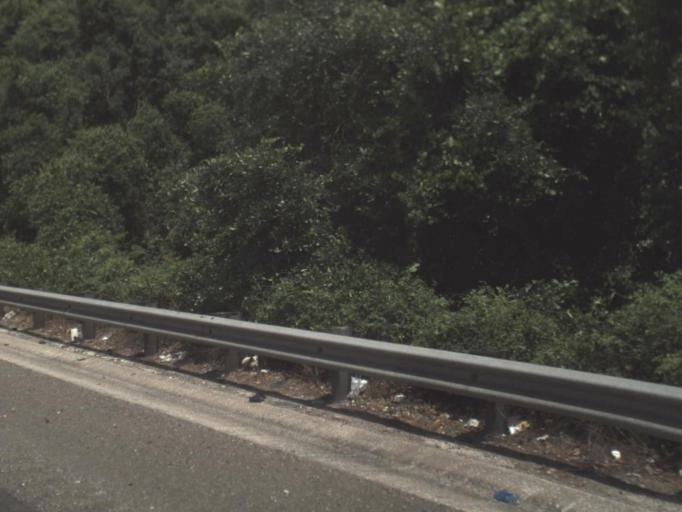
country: US
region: Florida
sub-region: Duval County
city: Jacksonville
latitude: 30.3271
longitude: -81.7669
